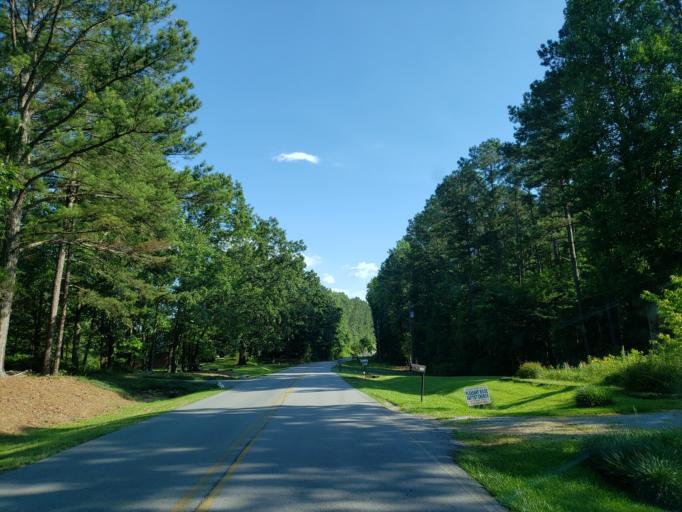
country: US
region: Georgia
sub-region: Carroll County
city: Carrollton
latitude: 33.6621
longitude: -85.0856
